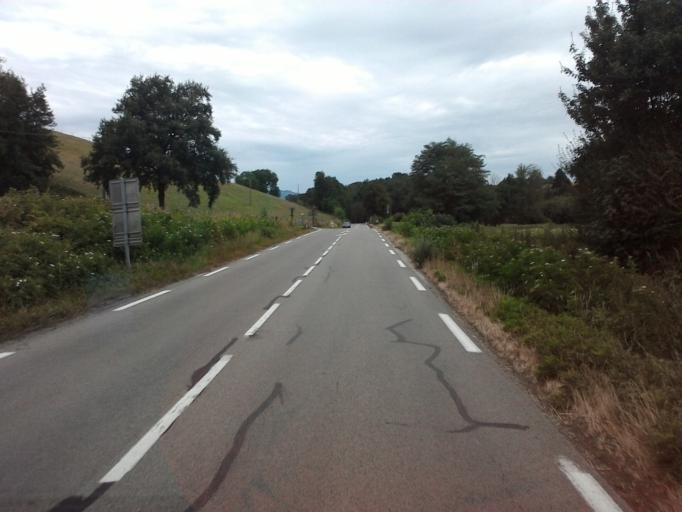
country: FR
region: Rhone-Alpes
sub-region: Departement de l'Isere
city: Corbelin
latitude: 45.6012
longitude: 5.5348
